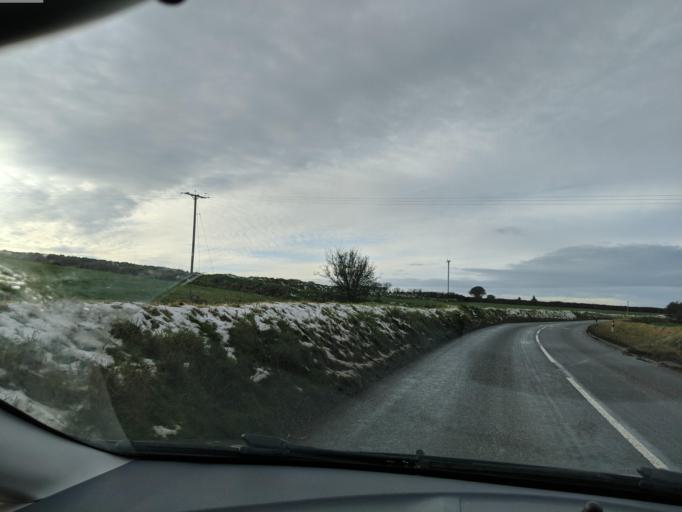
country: GB
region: England
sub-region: Cornwall
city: Jacobstow
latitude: 50.6641
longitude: -4.5889
